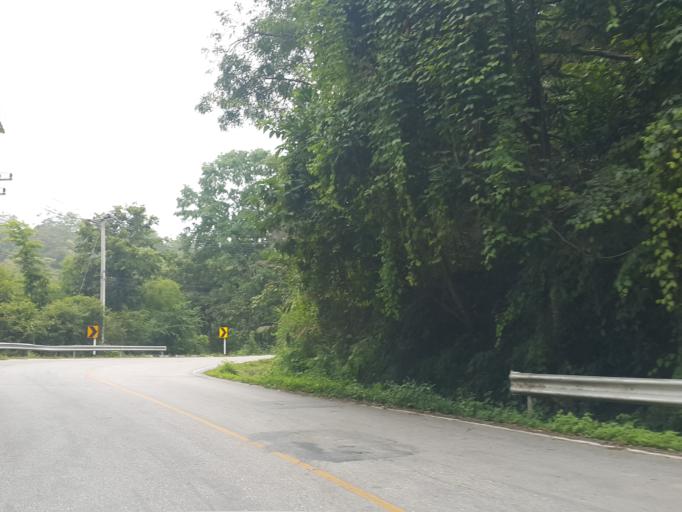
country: TH
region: Mae Hong Son
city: Mae Hi
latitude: 19.2654
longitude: 98.5057
